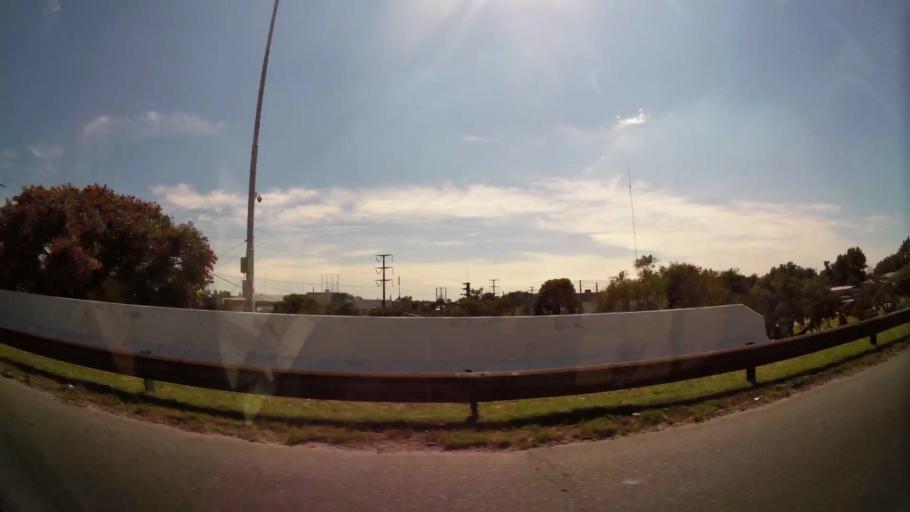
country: AR
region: Buenos Aires
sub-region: Partido de Tigre
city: Tigre
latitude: -34.4414
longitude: -58.5821
